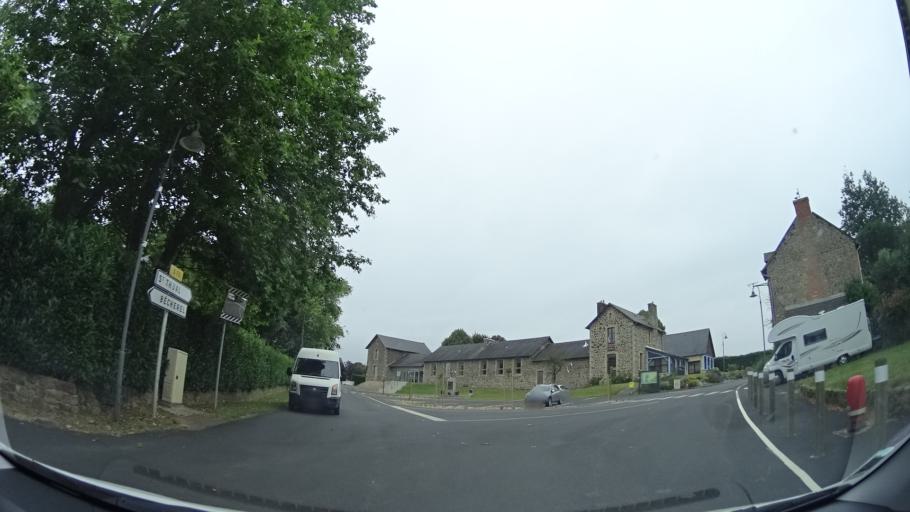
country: FR
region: Brittany
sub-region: Departement d'Ille-et-Vilaine
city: Irodouer
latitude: 48.3093
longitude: -1.9395
